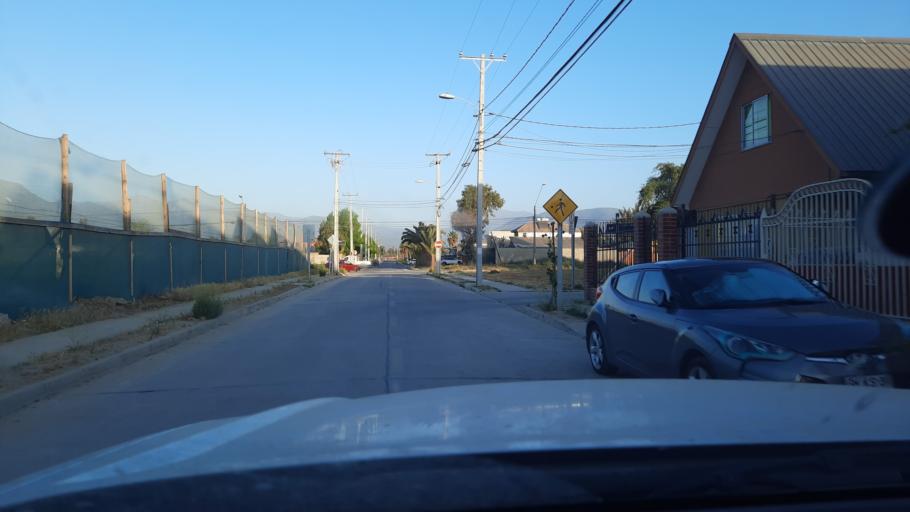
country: CL
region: Valparaiso
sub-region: Provincia de Marga Marga
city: Limache
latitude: -32.9958
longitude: -71.2762
